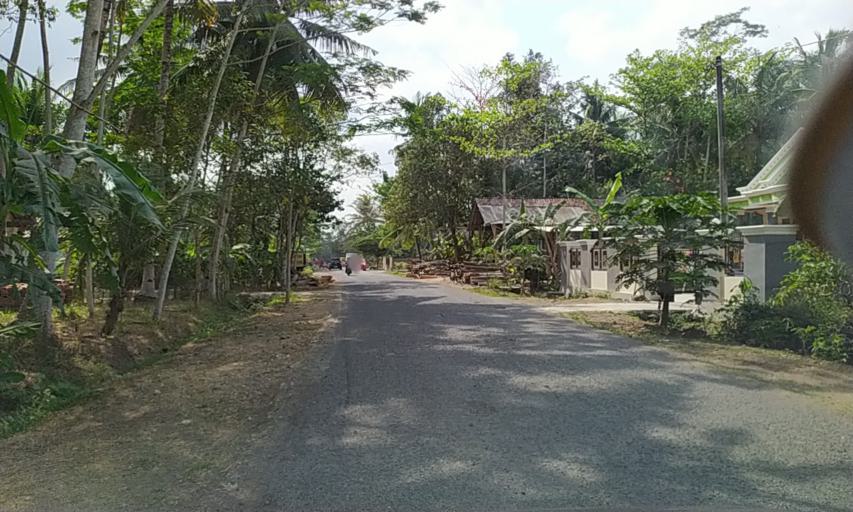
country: ID
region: Central Java
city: Citengah
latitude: -7.4866
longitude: 108.7769
